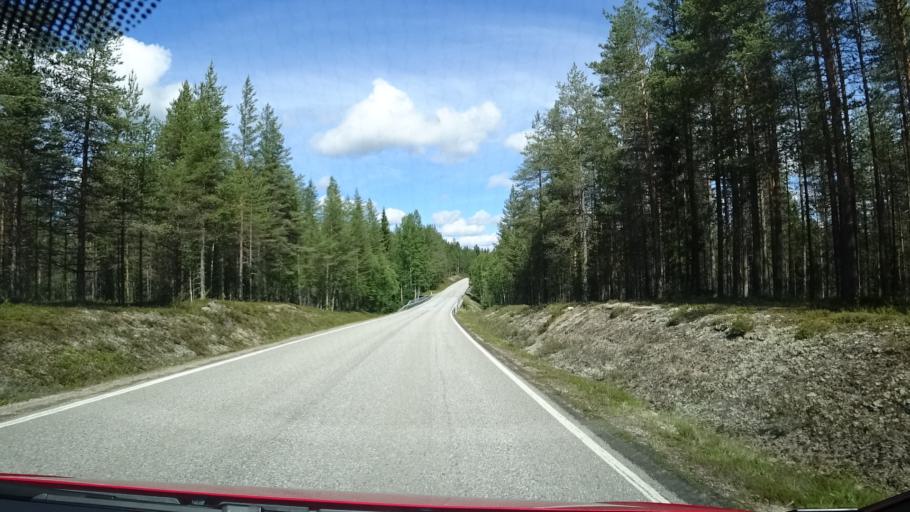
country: FI
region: Kainuu
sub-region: Kehys-Kainuu
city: Kuhmo
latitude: 64.6999
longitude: 29.6750
